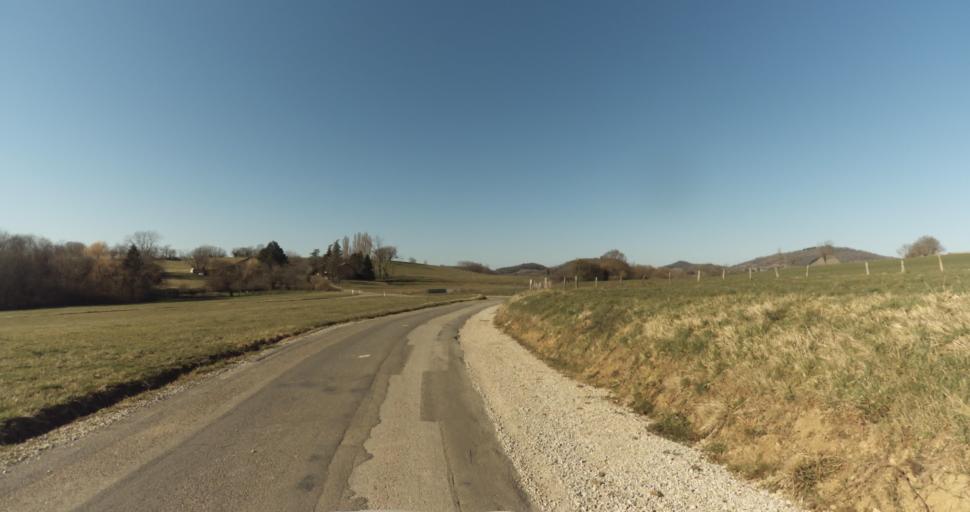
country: FR
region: Franche-Comte
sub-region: Departement du Jura
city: Montmorot
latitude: 46.6893
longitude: 5.5355
